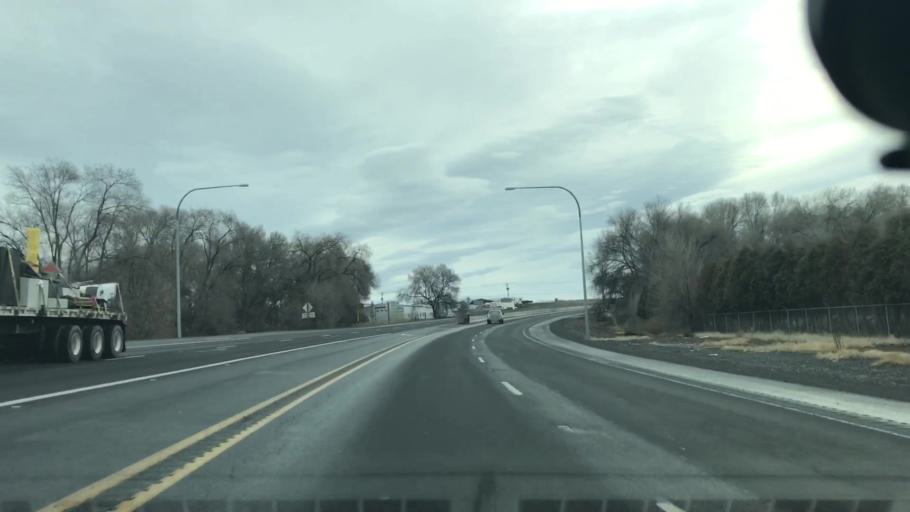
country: US
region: Washington
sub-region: Grant County
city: Moses Lake
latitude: 47.1392
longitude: -119.2610
